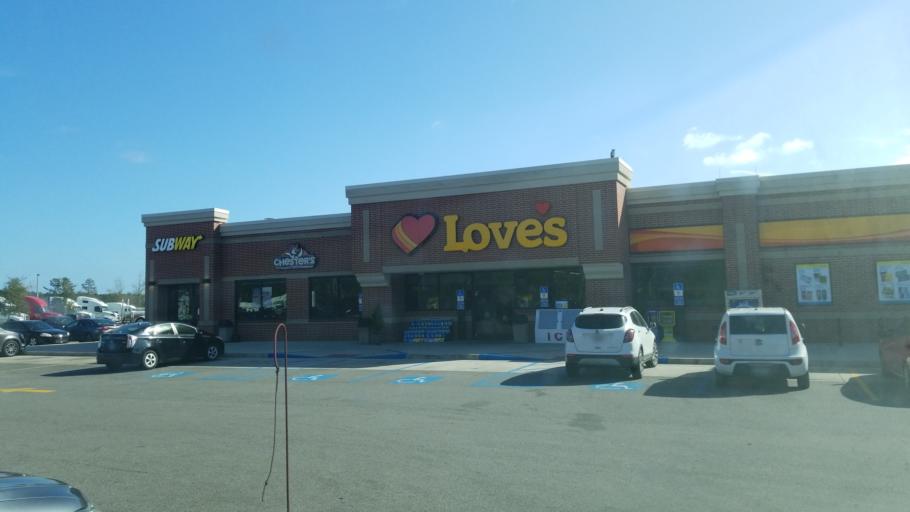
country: US
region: Florida
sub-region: Nassau County
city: Yulee
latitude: 30.5170
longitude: -81.6331
